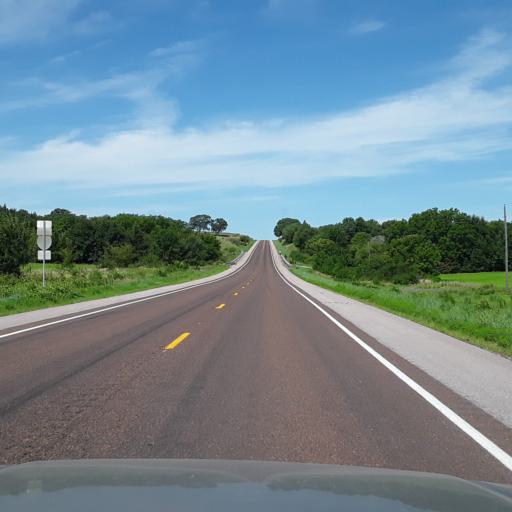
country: US
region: Nebraska
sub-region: Seward County
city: Milford
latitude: 40.8865
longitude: -96.9120
